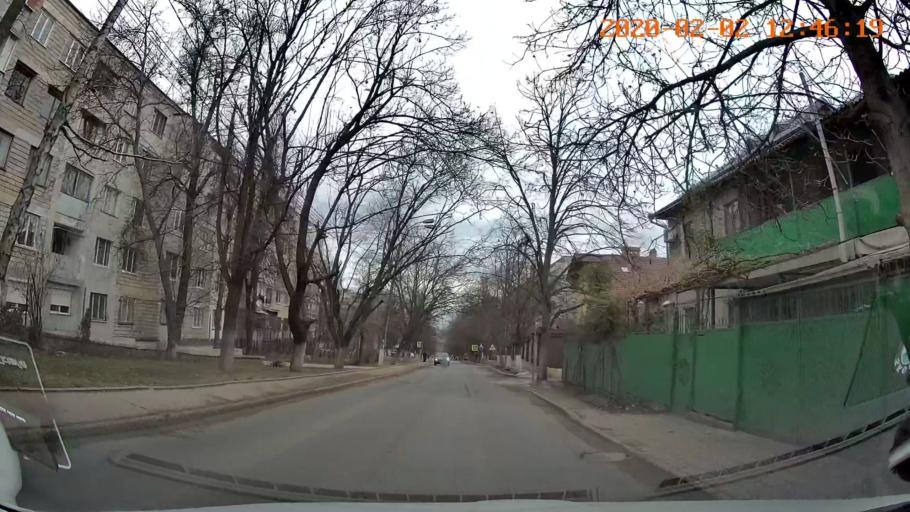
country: MD
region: Chisinau
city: Chisinau
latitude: 47.0084
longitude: 28.8172
